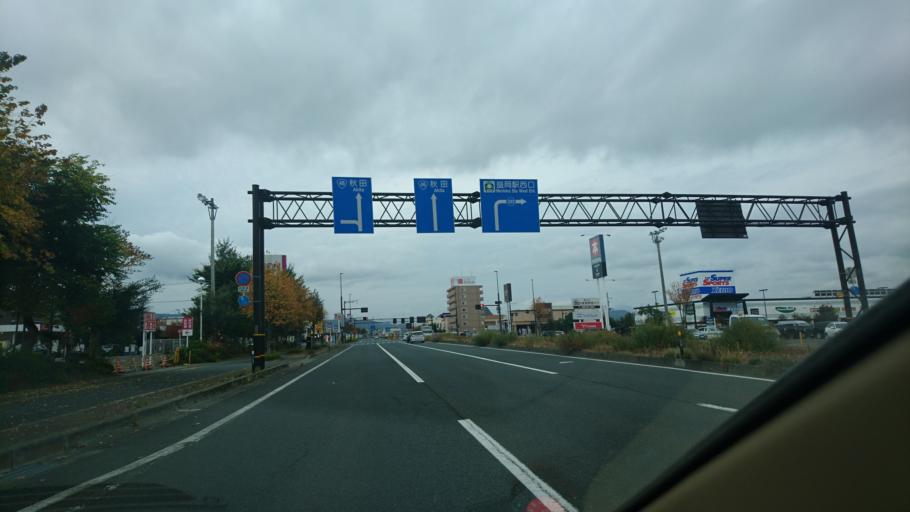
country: JP
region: Iwate
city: Morioka-shi
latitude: 39.6850
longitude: 141.1279
